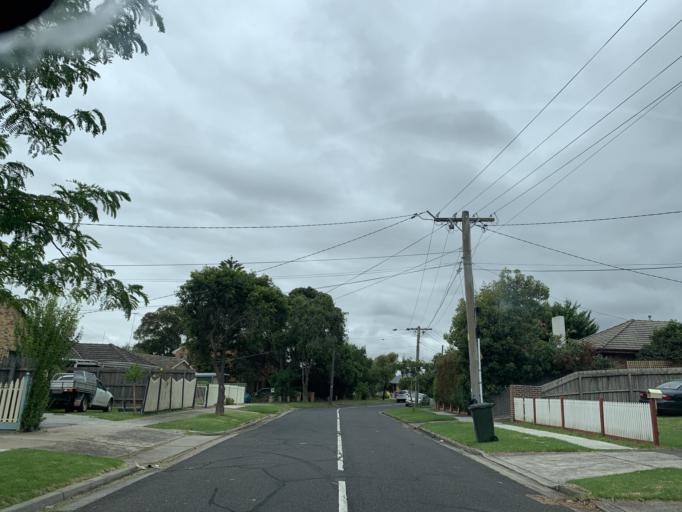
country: AU
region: Victoria
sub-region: Hume
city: Jacana
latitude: -37.6879
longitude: 144.9077
